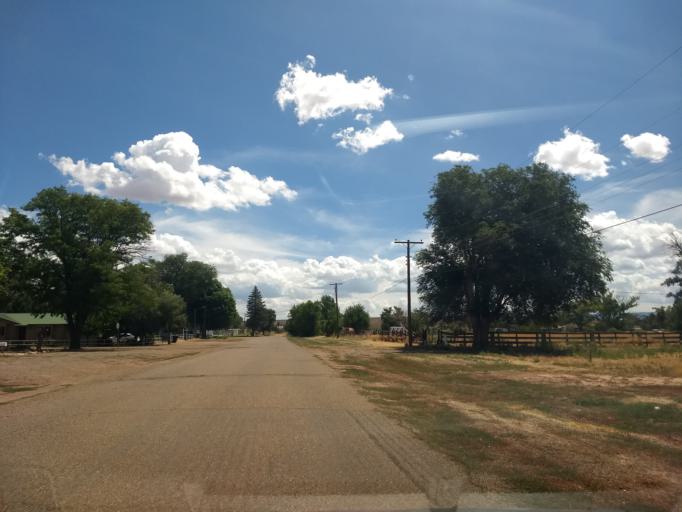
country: US
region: Arizona
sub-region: Coconino County
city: Fredonia
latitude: 36.9490
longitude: -112.5237
